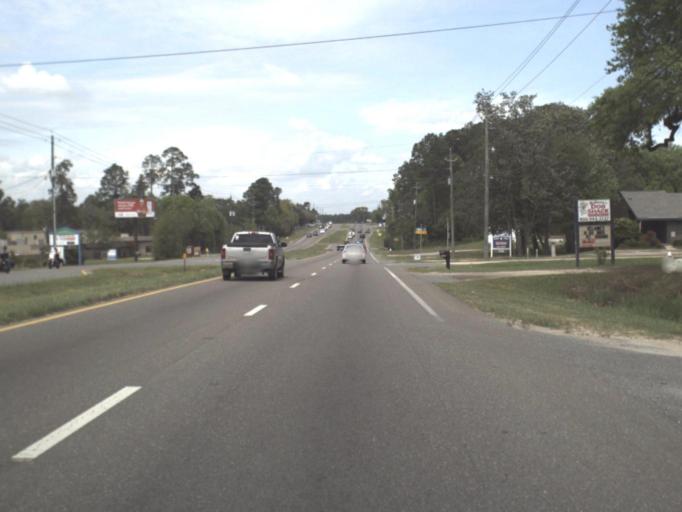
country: US
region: Florida
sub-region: Escambia County
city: Bellview
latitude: 30.4954
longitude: -87.3060
